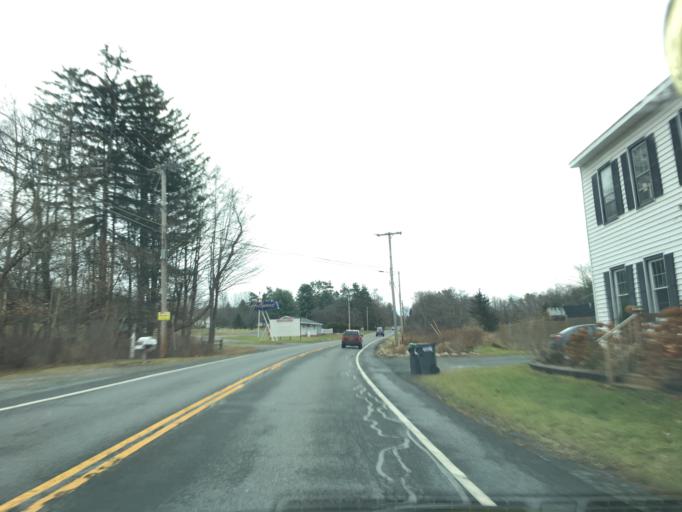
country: US
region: New York
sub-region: Rensselaer County
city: Poestenkill
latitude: 42.6766
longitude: -73.5967
